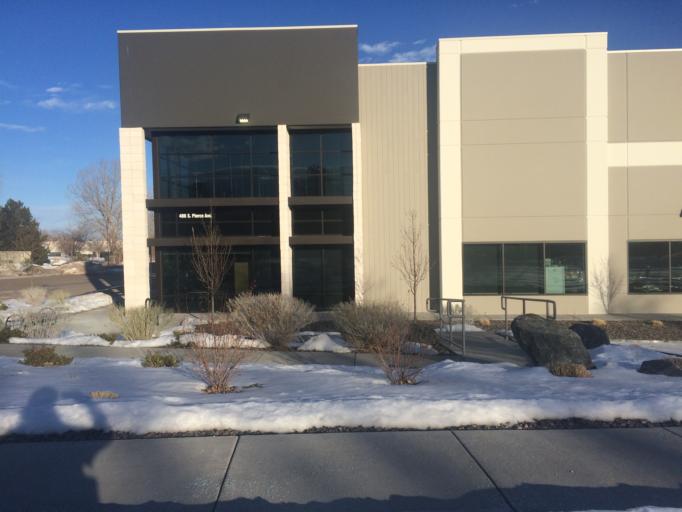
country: US
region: Colorado
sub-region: Boulder County
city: Louisville
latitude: 39.9637
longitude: -105.1221
